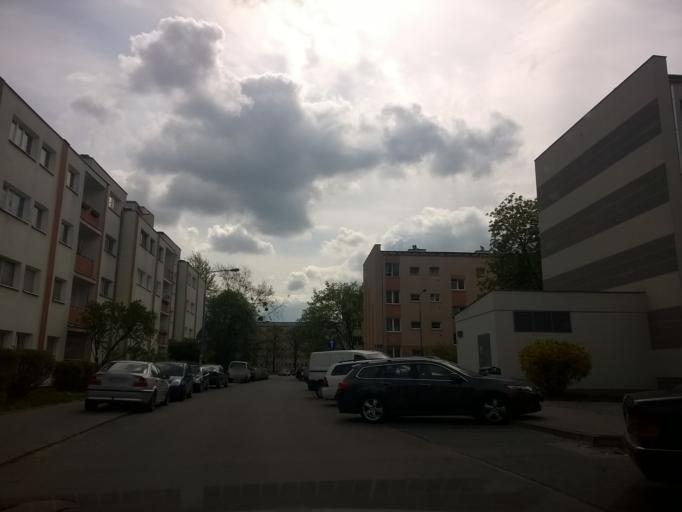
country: PL
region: Masovian Voivodeship
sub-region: Warszawa
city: Mokotow
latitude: 52.1902
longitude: 21.0124
